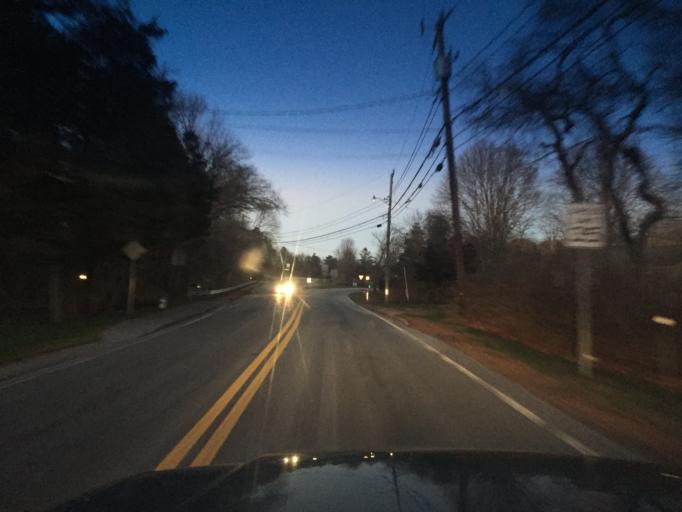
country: US
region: Massachusetts
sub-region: Barnstable County
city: North Falmouth
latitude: 41.6312
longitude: -70.6186
